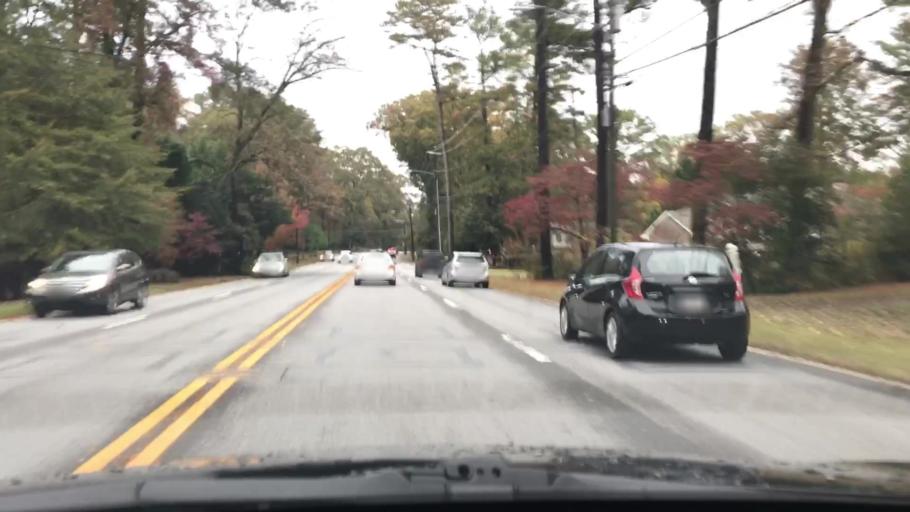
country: US
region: Georgia
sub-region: DeKalb County
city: North Druid Hills
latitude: 33.8163
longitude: -84.3059
